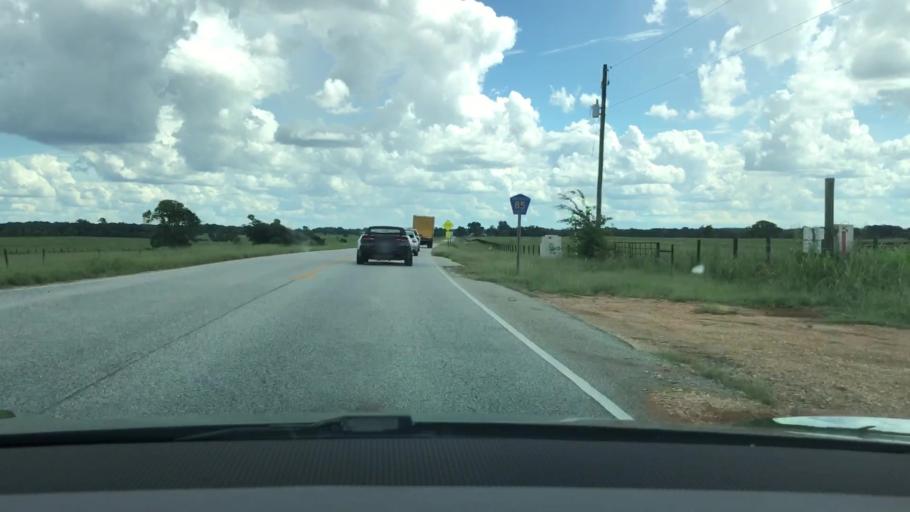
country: US
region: Alabama
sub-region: Montgomery County
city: Pike Road
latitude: 32.2729
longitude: -86.0998
